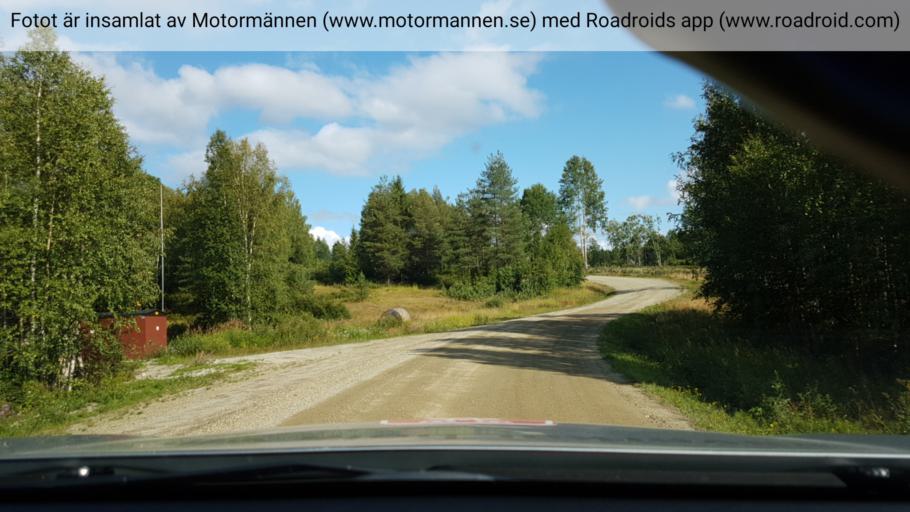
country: SE
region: Vaesterbotten
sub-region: Lycksele Kommun
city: Lycksele
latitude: 64.5794
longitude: 19.0324
